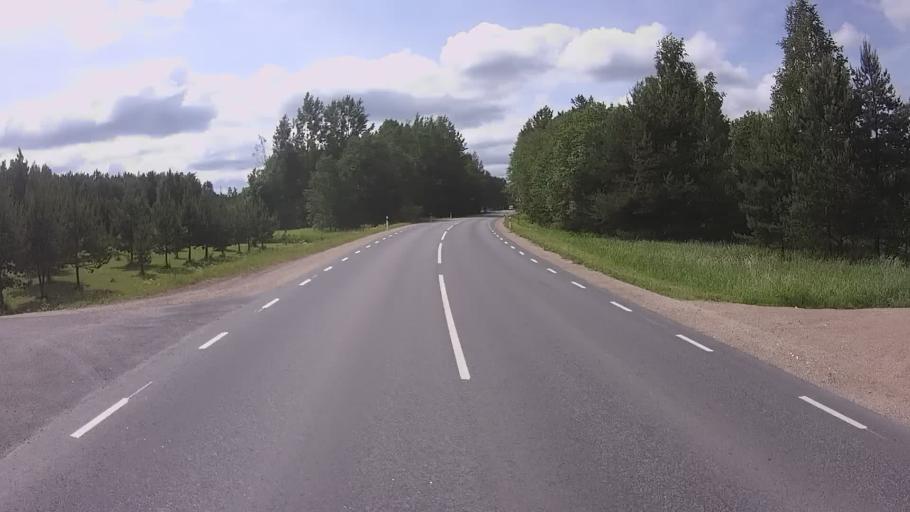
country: EE
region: Polvamaa
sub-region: Polva linn
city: Polva
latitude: 58.0634
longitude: 27.0818
